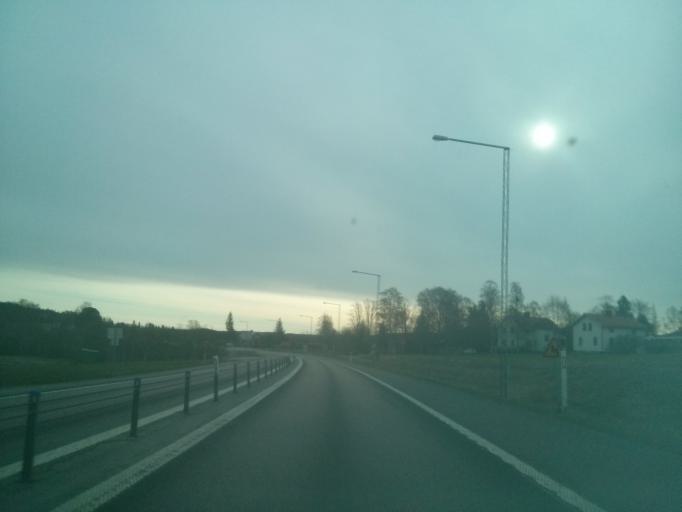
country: SE
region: Vaesternorrland
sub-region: Haernoesands Kommun
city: Haernoesand
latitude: 62.6107
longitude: 17.8792
